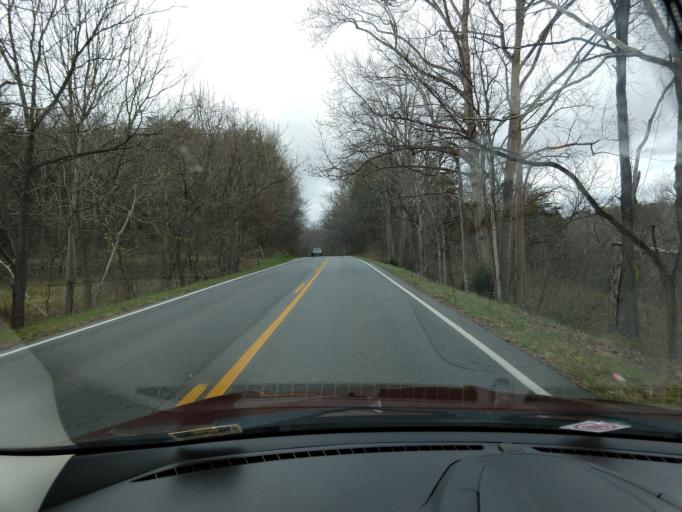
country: US
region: Virginia
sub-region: Botetourt County
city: Blue Ridge
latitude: 37.2648
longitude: -79.7567
